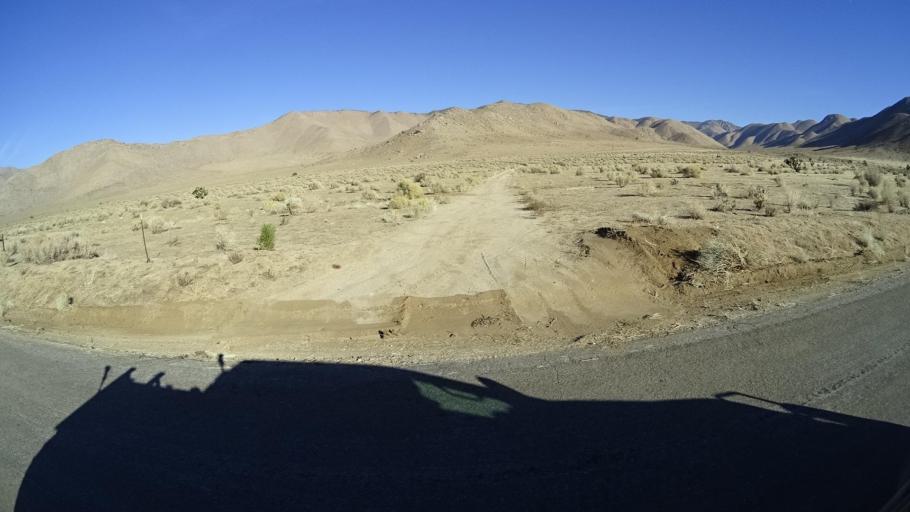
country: US
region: California
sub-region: Kern County
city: Weldon
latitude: 35.6012
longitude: -118.2415
